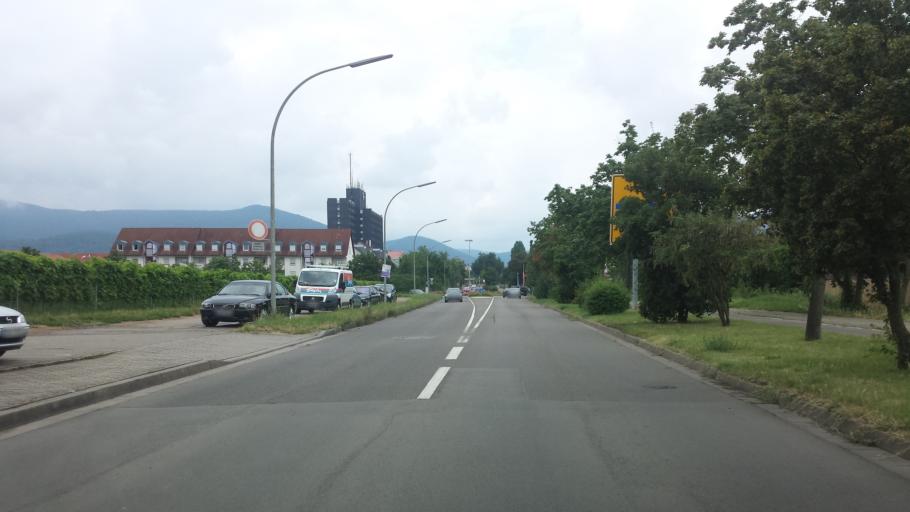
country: DE
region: Rheinland-Pfalz
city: Neustadt
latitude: 49.3448
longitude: 8.1652
